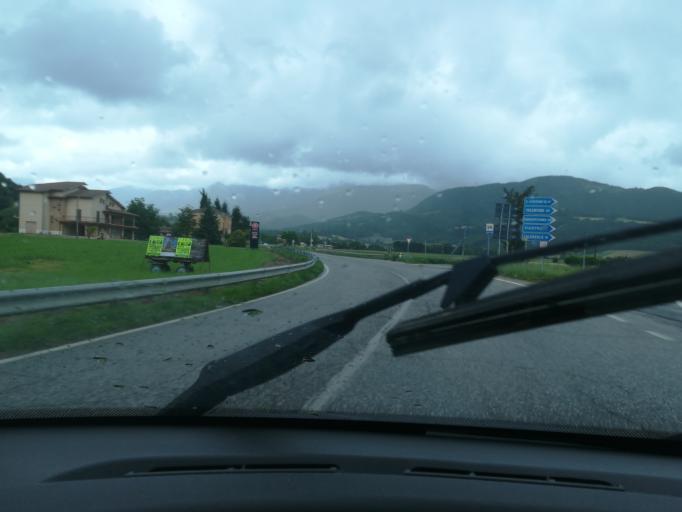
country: IT
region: The Marches
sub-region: Provincia di Macerata
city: Cessapalombo
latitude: 43.0766
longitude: 13.2801
